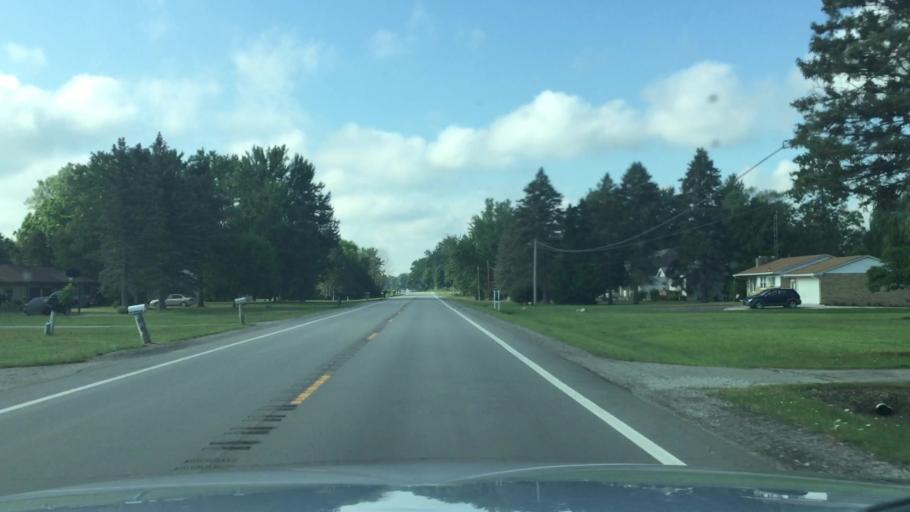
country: US
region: Michigan
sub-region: Genesee County
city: Clio
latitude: 43.2250
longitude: -83.7352
